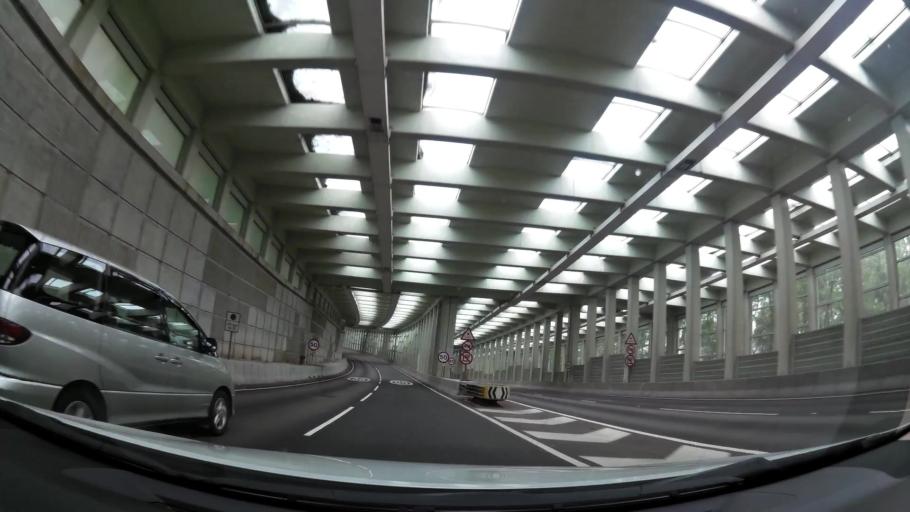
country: HK
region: Tsuen Wan
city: Tsuen Wan
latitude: 22.3756
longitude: 114.1177
